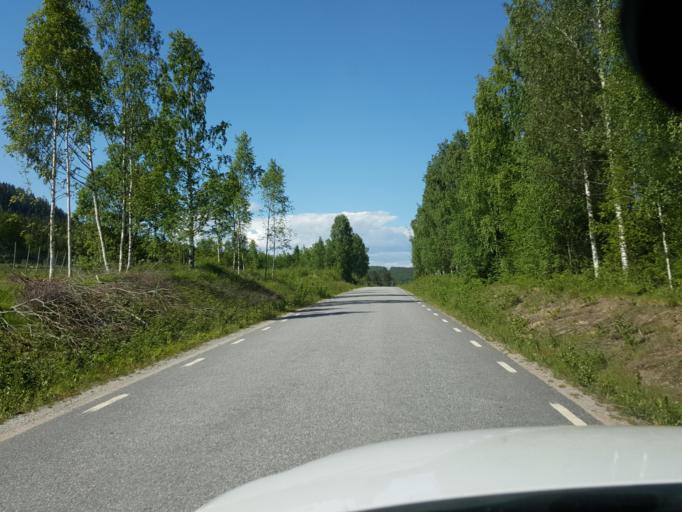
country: SE
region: Gaevleborg
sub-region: Ljusdals Kommun
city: Jaervsoe
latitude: 61.7322
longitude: 16.2830
